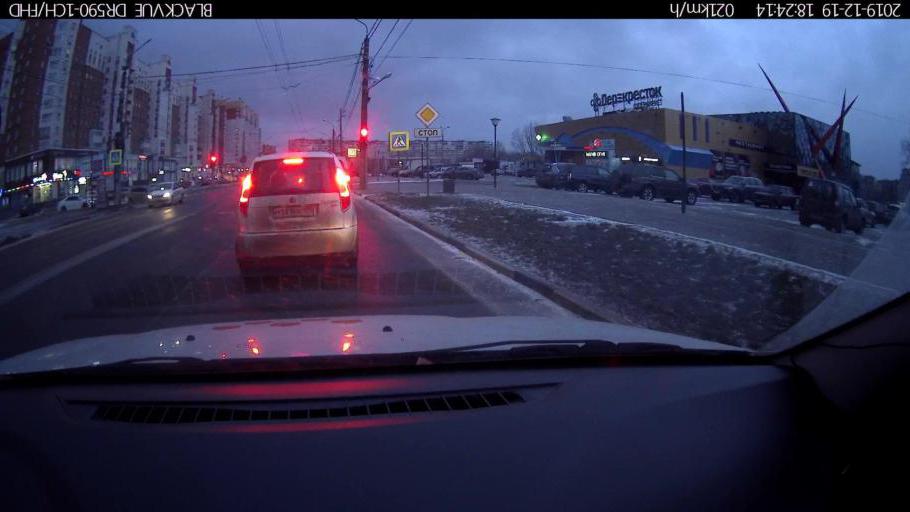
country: RU
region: Nizjnij Novgorod
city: Nizhniy Novgorod
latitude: 56.3384
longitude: 43.9358
